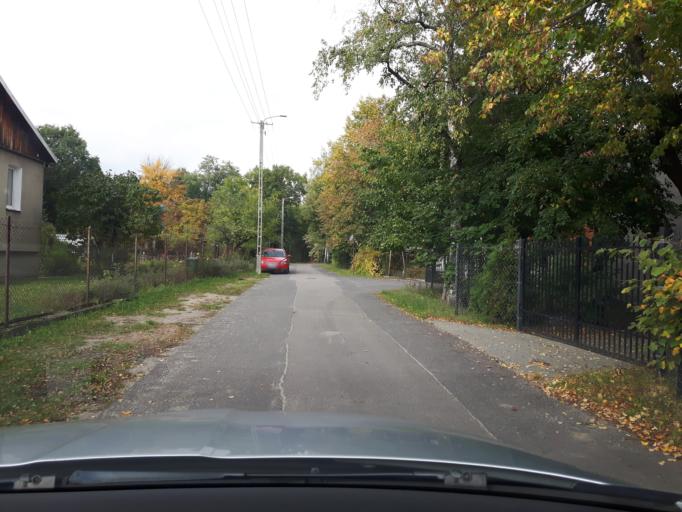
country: PL
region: Masovian Voivodeship
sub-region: Powiat wolominski
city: Zabki
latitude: 52.2989
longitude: 21.1240
